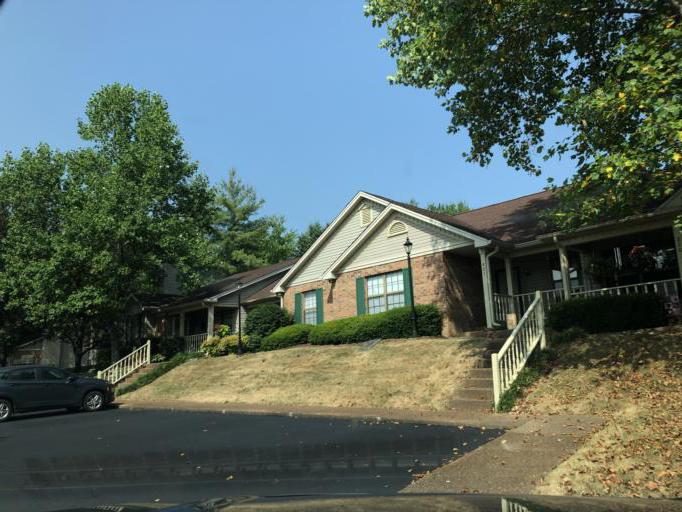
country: US
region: Tennessee
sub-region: Rutherford County
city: La Vergne
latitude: 36.0469
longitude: -86.6426
